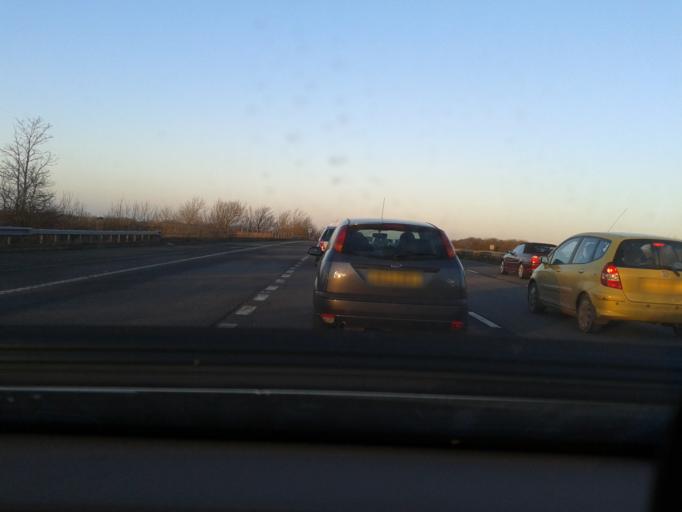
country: GB
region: England
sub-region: North Somerset
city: St. Georges
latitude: 51.3644
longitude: -2.8918
